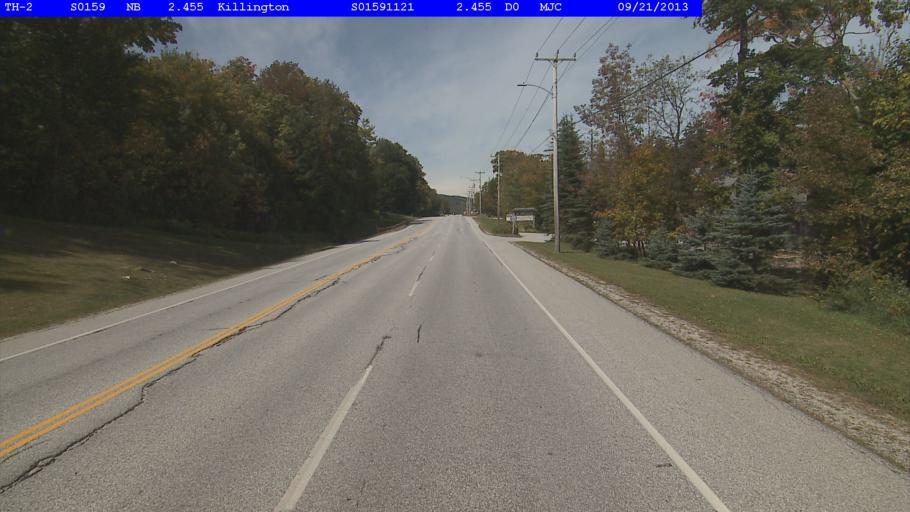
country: US
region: Vermont
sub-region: Rutland County
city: Rutland
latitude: 43.6617
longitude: -72.7980
